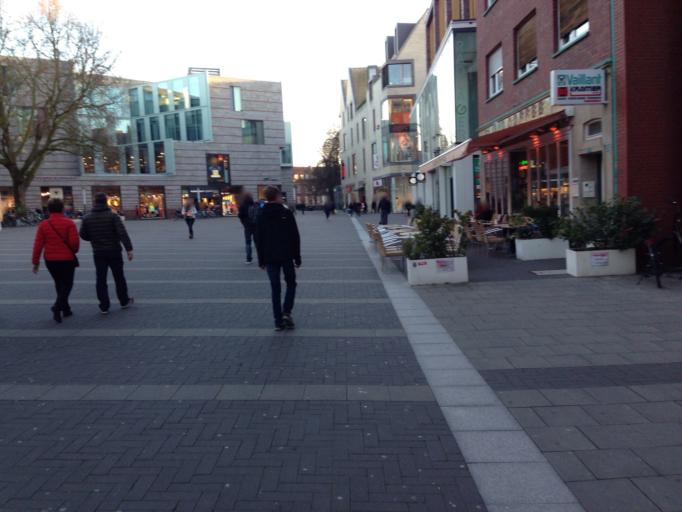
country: DE
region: North Rhine-Westphalia
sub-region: Regierungsbezirk Munster
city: Muenster
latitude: 51.9606
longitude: 7.6294
